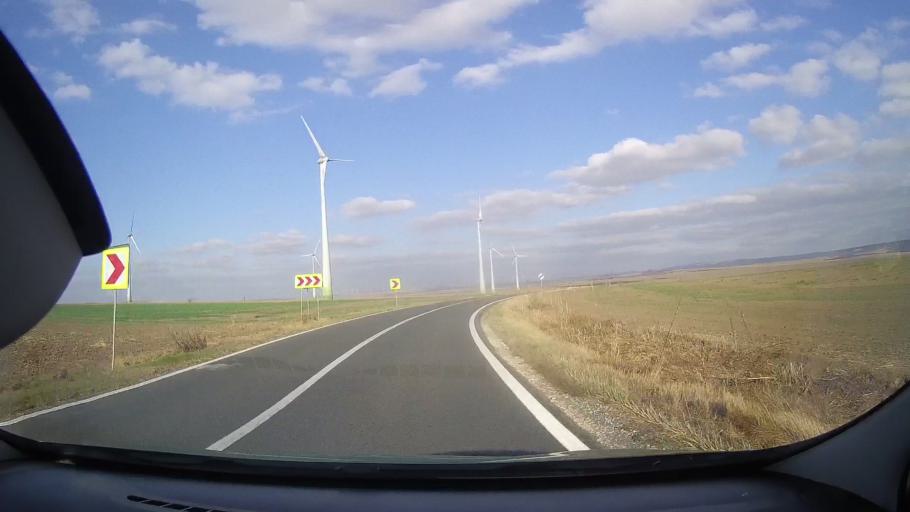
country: RO
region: Tulcea
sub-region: Comuna Topolog
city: Topolog
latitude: 44.8186
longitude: 28.2602
